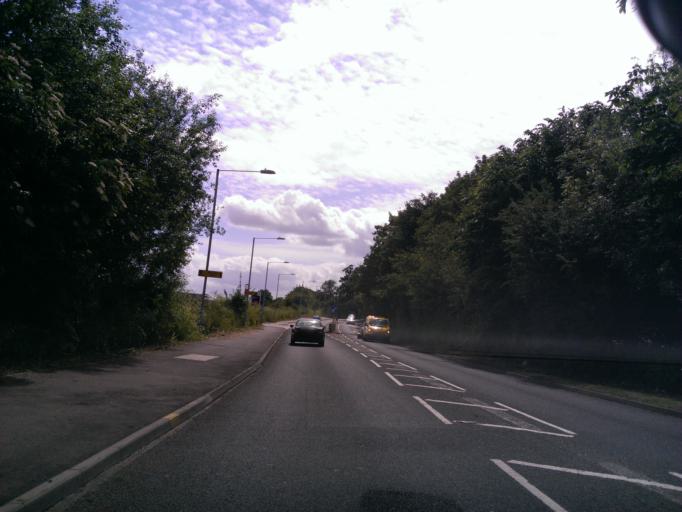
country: GB
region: England
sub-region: Essex
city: Witham
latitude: 51.7900
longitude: 0.6255
